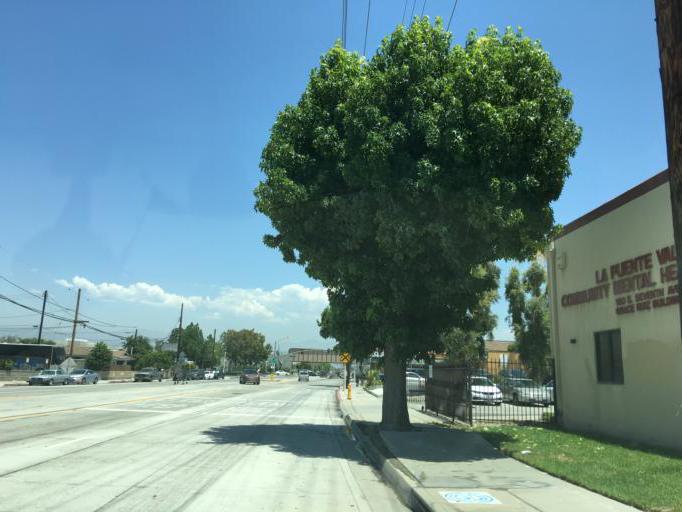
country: US
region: California
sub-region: Los Angeles County
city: Avocado Heights
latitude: 34.0335
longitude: -117.9761
